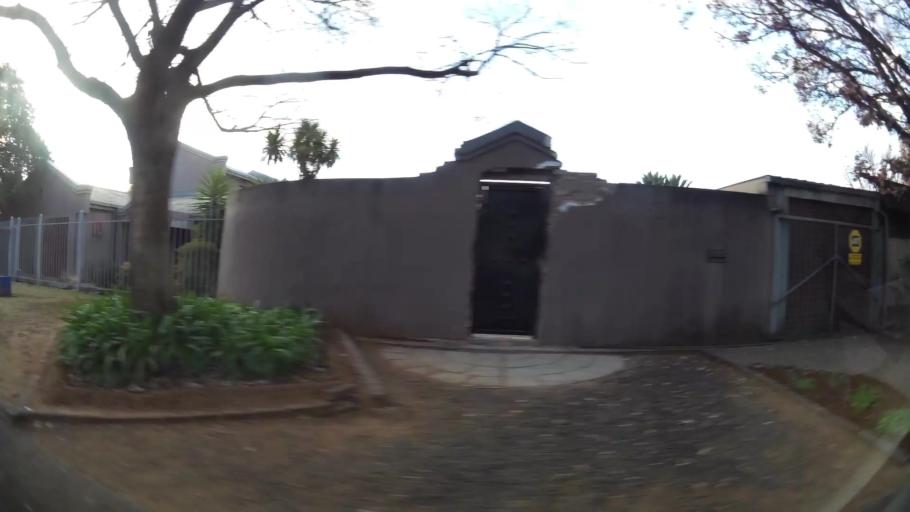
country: ZA
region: Orange Free State
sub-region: Mangaung Metropolitan Municipality
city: Bloemfontein
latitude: -29.1367
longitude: 26.1741
